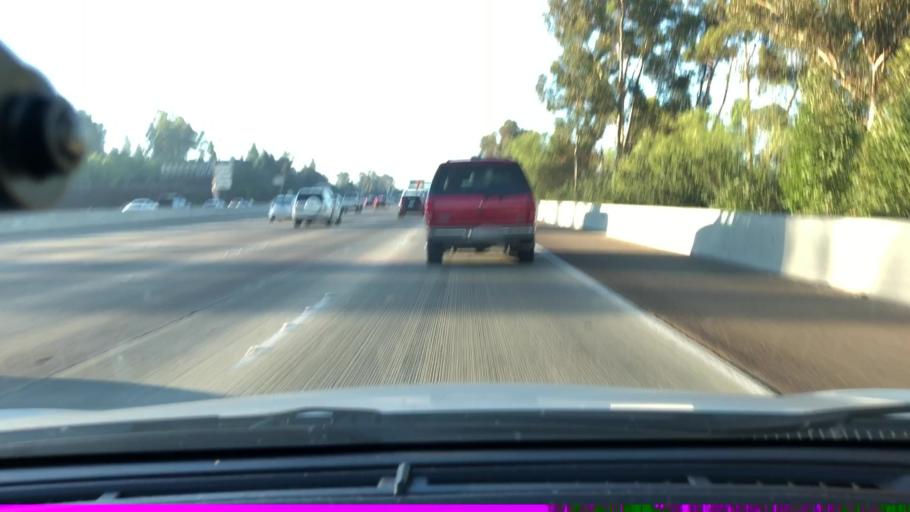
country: US
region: California
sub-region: San Diego County
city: Escondido
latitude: 33.0410
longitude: -117.0750
